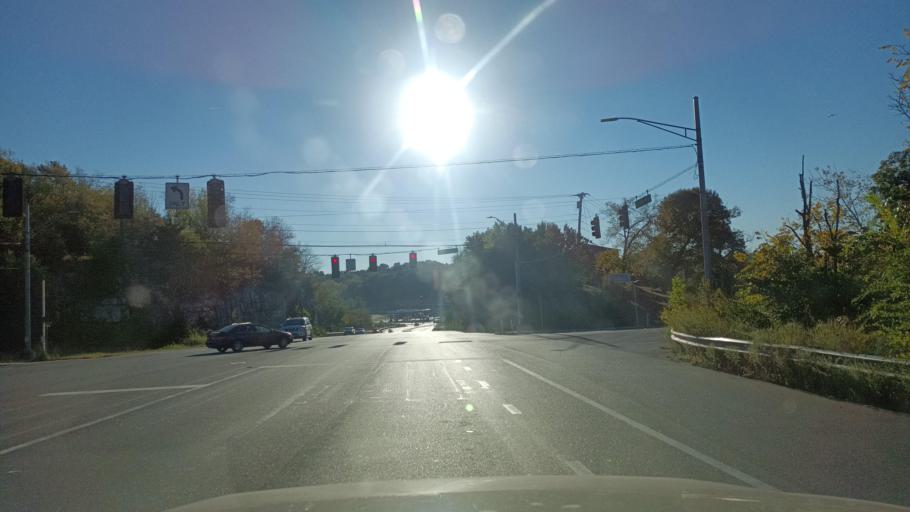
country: US
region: Missouri
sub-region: Boone County
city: Columbia
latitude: 38.9331
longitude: -92.3160
